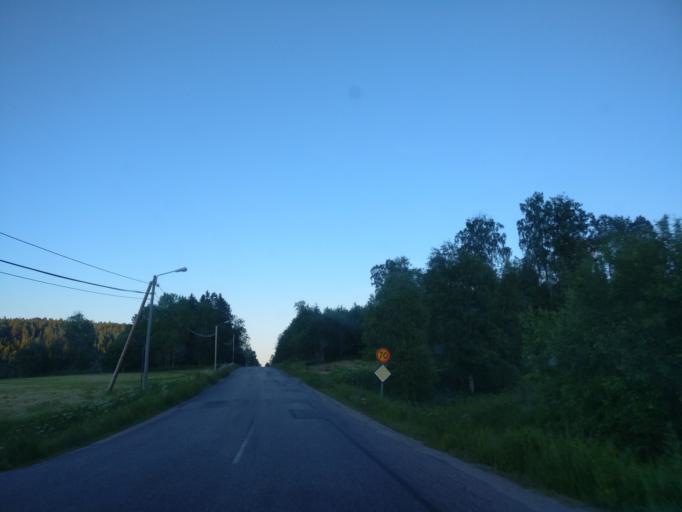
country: SE
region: Vaesternorrland
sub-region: Sundsvalls Kommun
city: Vi
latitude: 62.3132
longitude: 17.2000
